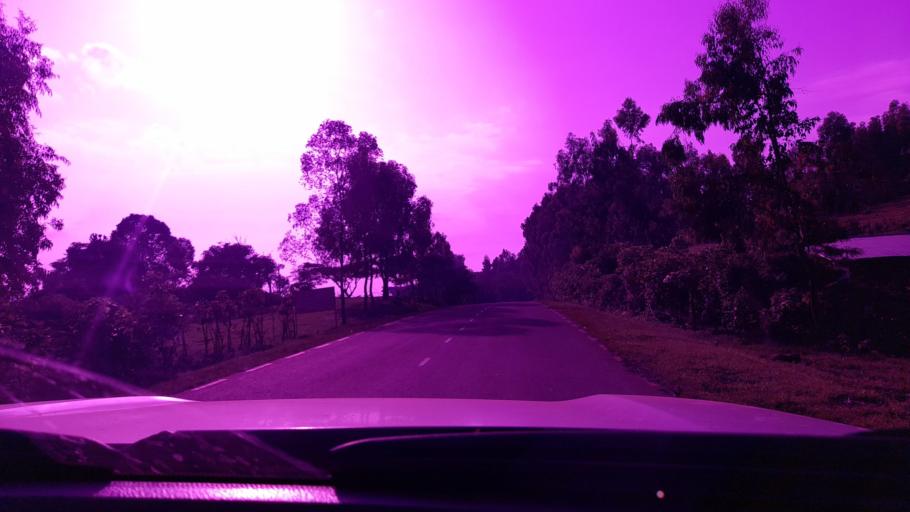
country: ET
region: Oromiya
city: Bedele
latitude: 8.1506
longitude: 36.4621
